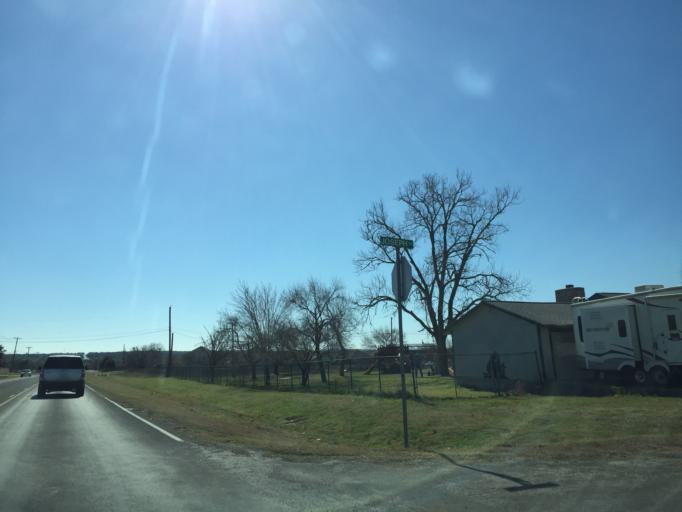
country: US
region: Texas
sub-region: Williamson County
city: Hutto
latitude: 30.5399
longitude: -97.6141
